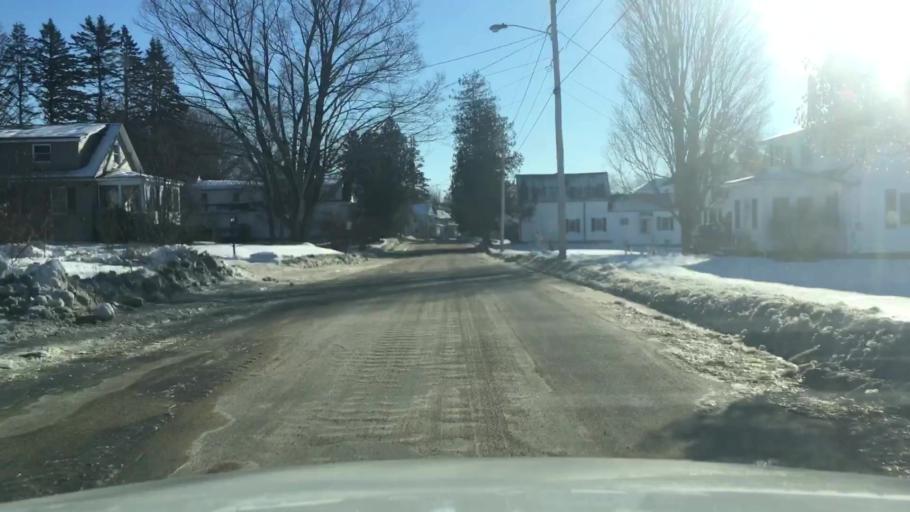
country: US
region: Maine
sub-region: Kennebec County
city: Winthrop
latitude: 44.3092
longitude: -69.9694
